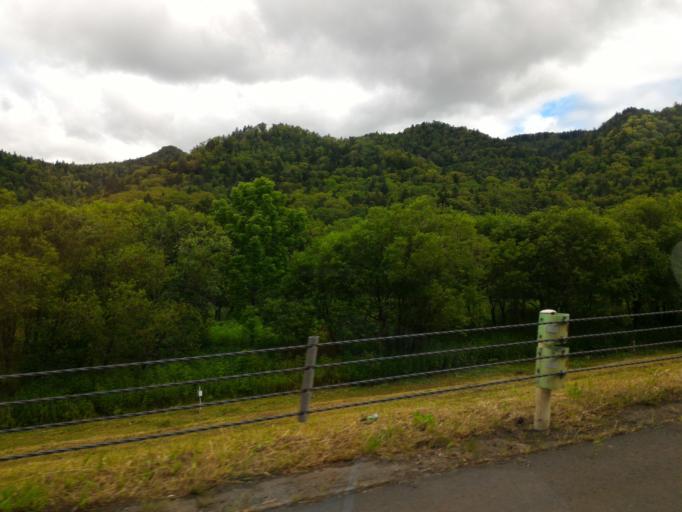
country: JP
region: Hokkaido
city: Nayoro
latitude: 44.7313
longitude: 142.2065
